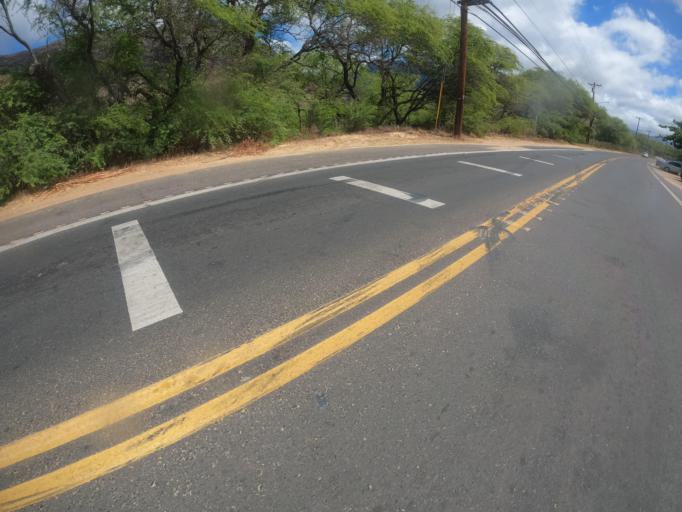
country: US
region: Hawaii
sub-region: Honolulu County
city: Makaha
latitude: 21.4780
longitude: -158.2213
